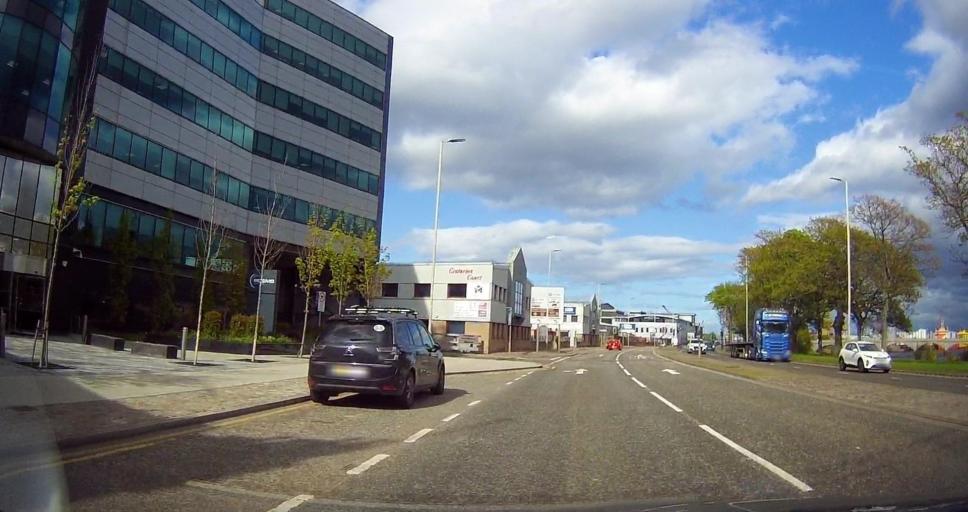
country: GB
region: Scotland
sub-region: Aberdeen City
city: Aberdeen
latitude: 57.1388
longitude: -2.0950
